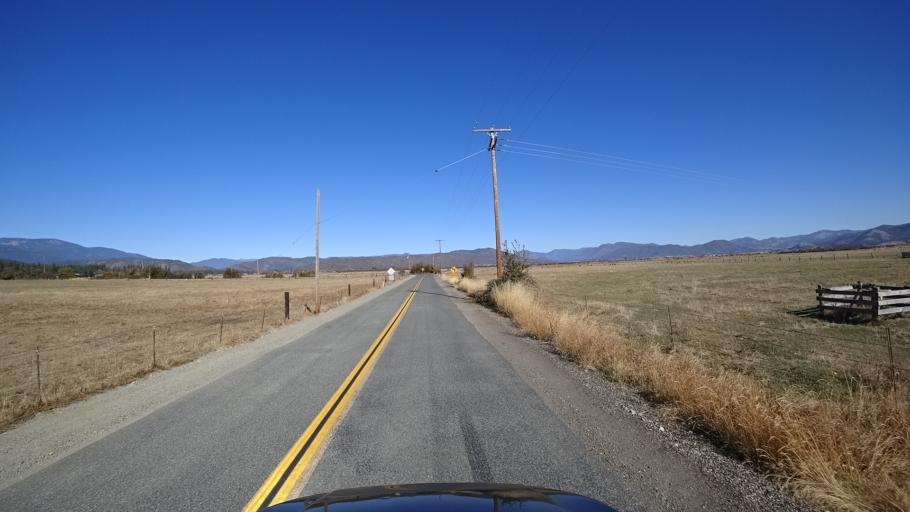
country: US
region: California
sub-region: Siskiyou County
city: Yreka
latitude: 41.5134
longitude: -122.8882
